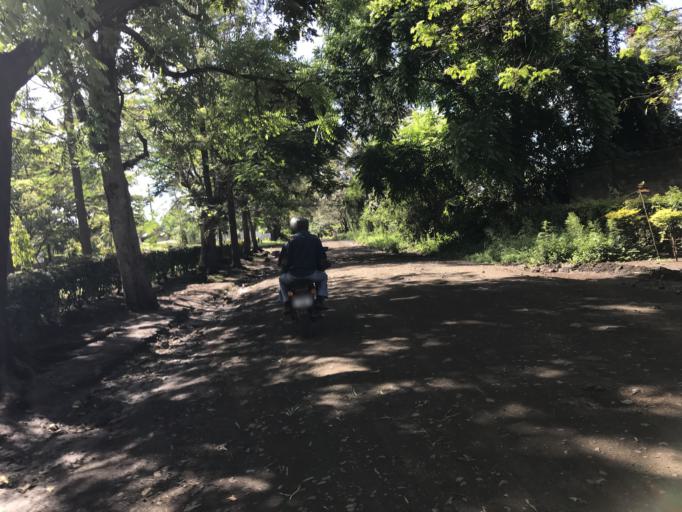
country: TZ
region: Arusha
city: Nkoaranga
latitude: -3.3850
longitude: 36.7962
